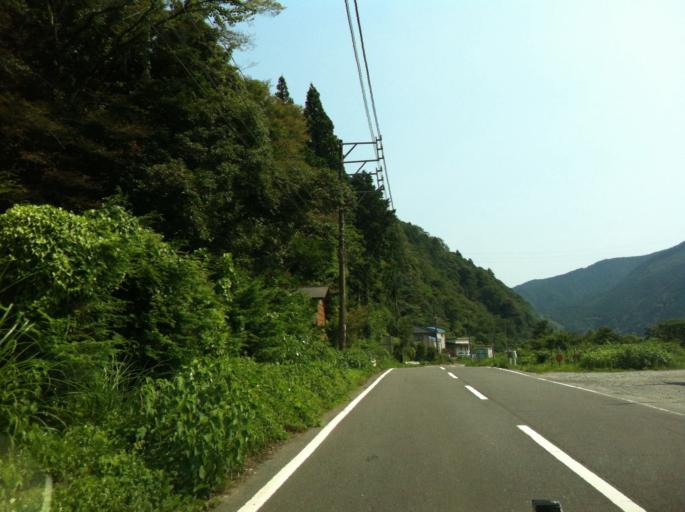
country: JP
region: Shizuoka
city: Shizuoka-shi
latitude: 35.1216
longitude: 138.3614
